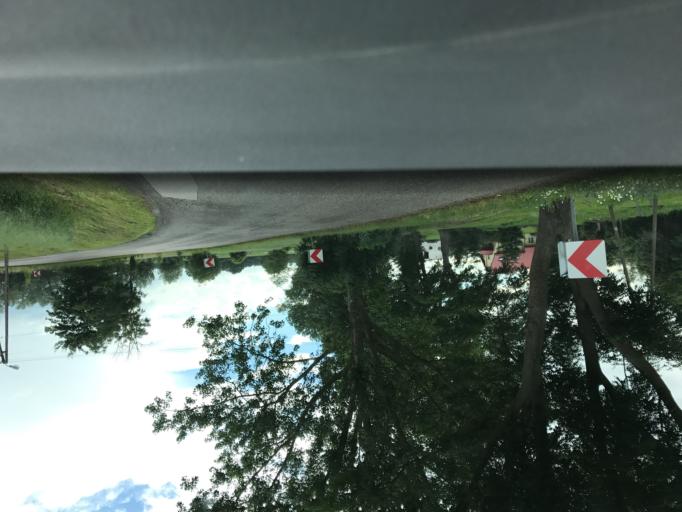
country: PL
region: Pomeranian Voivodeship
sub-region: Powiat gdanski
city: Suchy Dab
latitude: 54.2571
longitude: 18.7449
